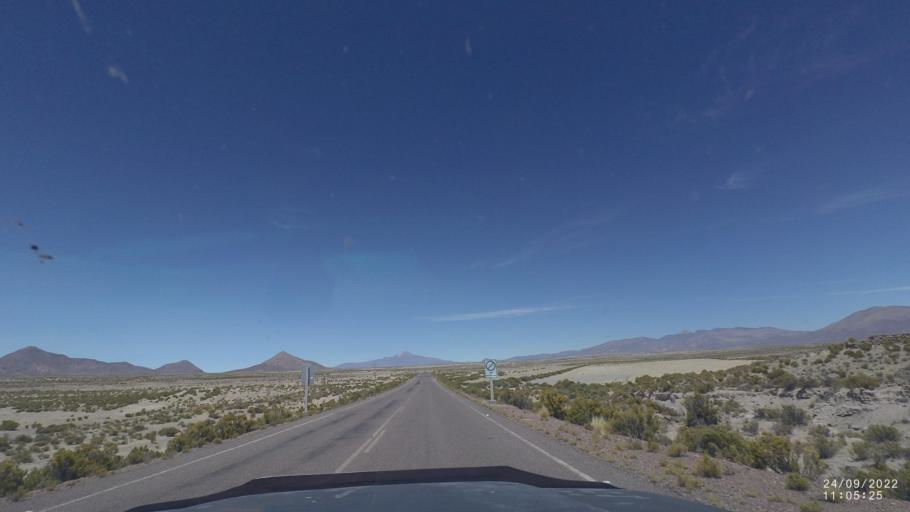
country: BO
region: Oruro
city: Challapata
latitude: -19.4736
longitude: -67.4292
